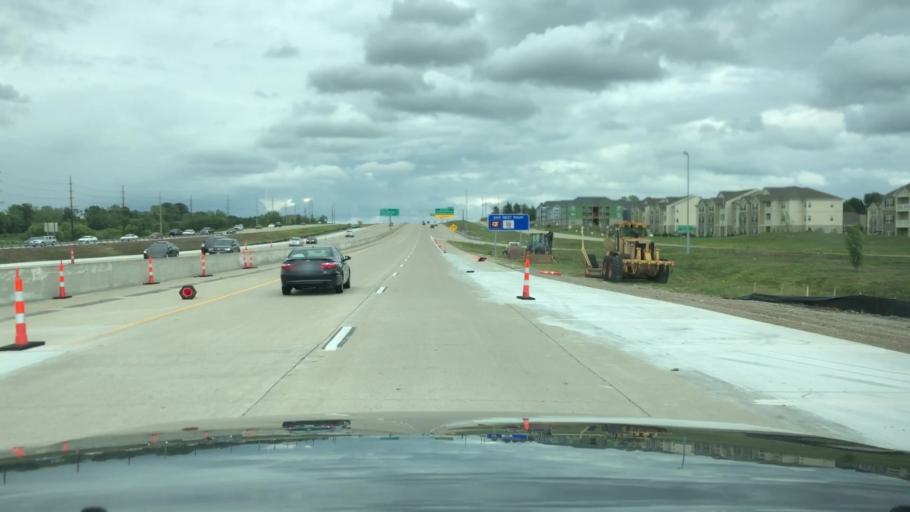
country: US
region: Missouri
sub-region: Saint Charles County
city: Cottleville
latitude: 38.7381
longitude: -90.6312
